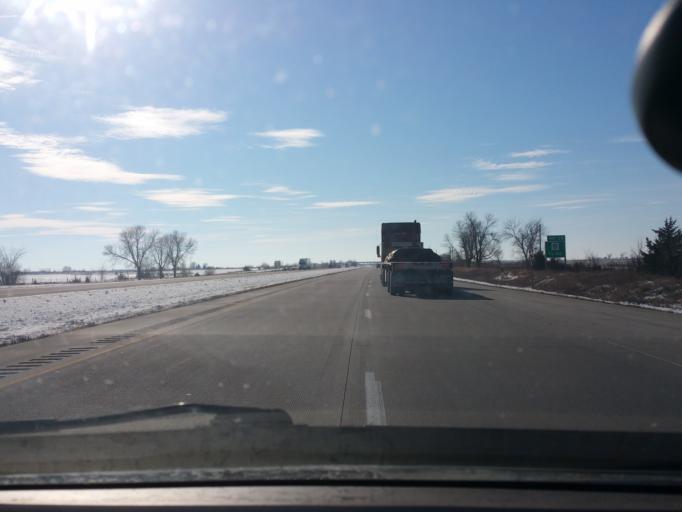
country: US
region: Iowa
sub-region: Clarke County
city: Osceola
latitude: 40.9860
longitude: -93.7978
